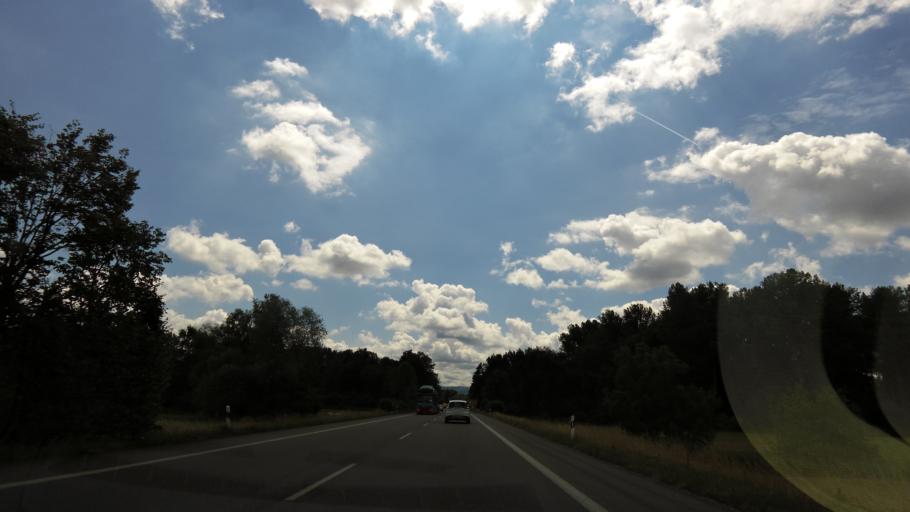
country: DE
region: Baden-Wuerttemberg
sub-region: Karlsruhe Region
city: Iffezheim
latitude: 48.8123
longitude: 8.1347
